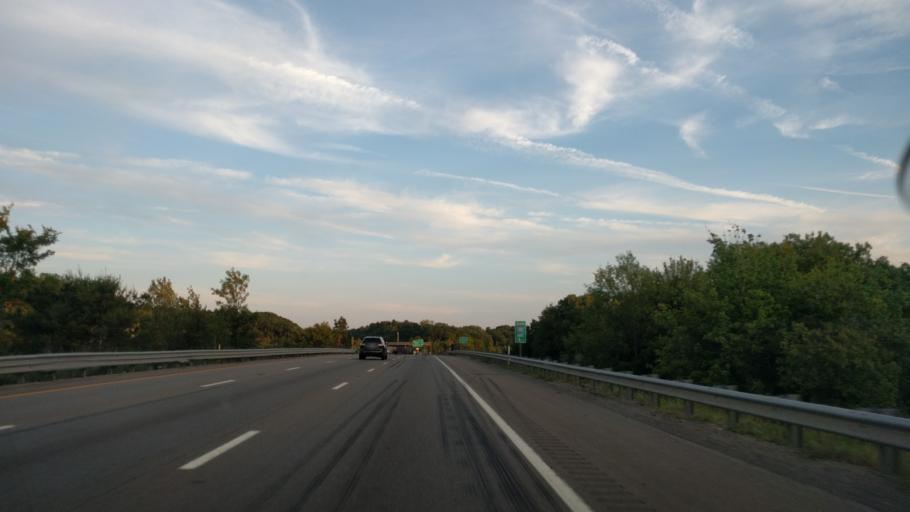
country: US
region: Massachusetts
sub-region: Worcester County
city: Cordaville
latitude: 42.2681
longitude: -71.5648
